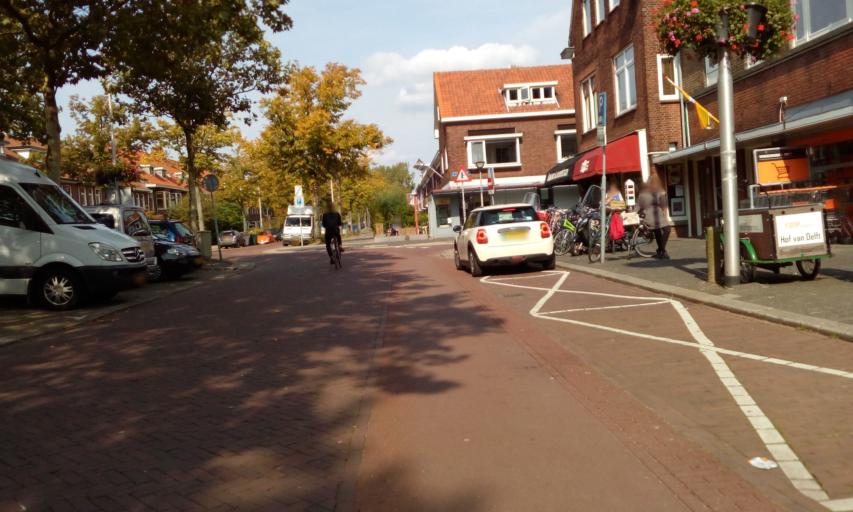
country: NL
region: South Holland
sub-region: Gemeente Delft
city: Delft
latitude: 52.0122
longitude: 4.3477
